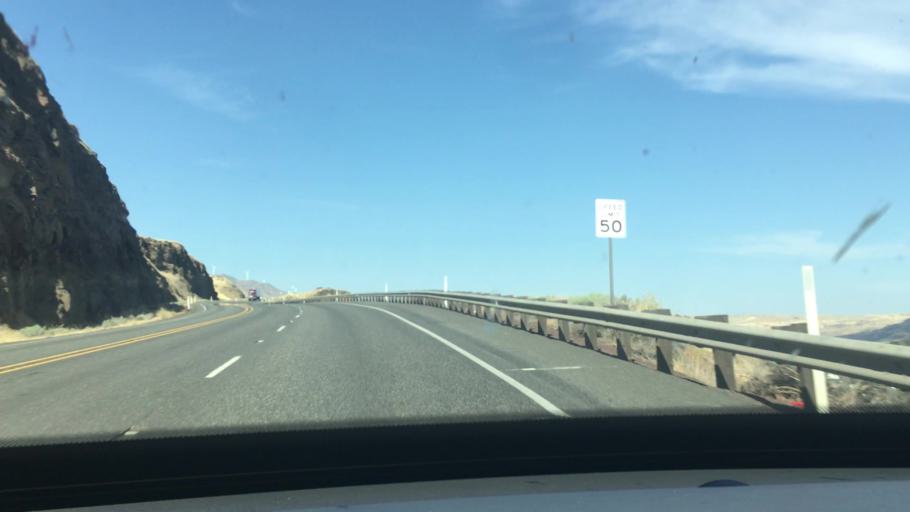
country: US
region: Washington
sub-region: Klickitat County
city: Goldendale
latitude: 45.6871
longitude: -120.8256
